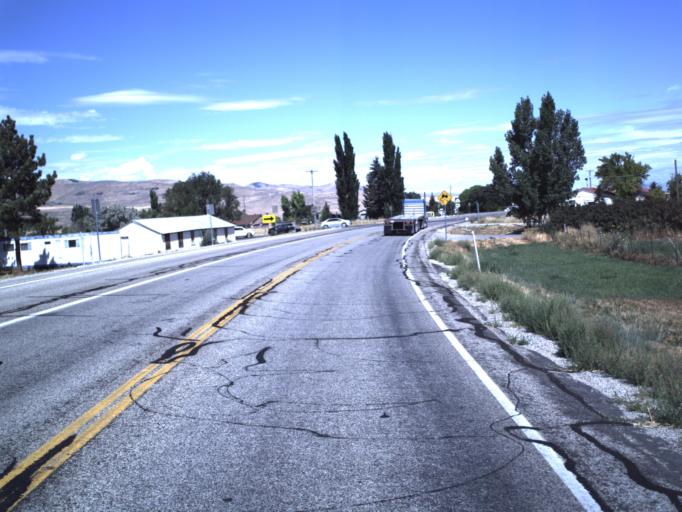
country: US
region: Utah
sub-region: Box Elder County
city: Garland
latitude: 41.7469
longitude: -112.1473
